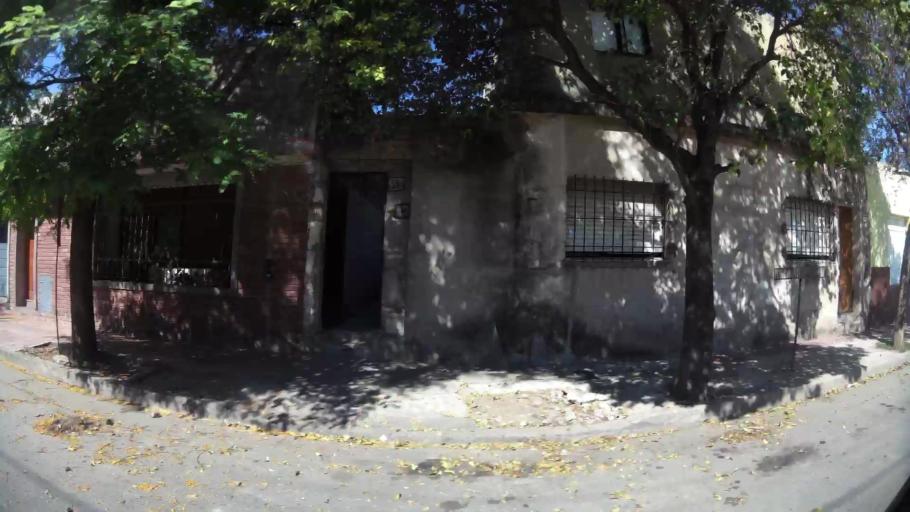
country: AR
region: Cordoba
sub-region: Departamento de Capital
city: Cordoba
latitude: -31.4150
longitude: -64.1577
